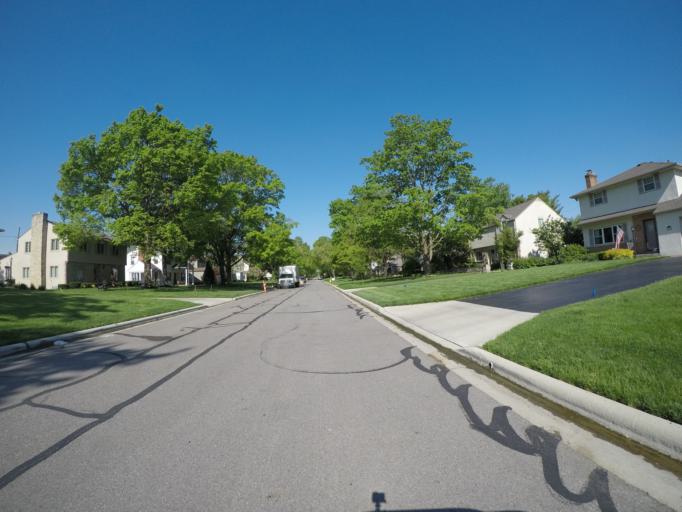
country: US
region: Ohio
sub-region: Franklin County
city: Upper Arlington
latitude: 40.0134
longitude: -83.0710
